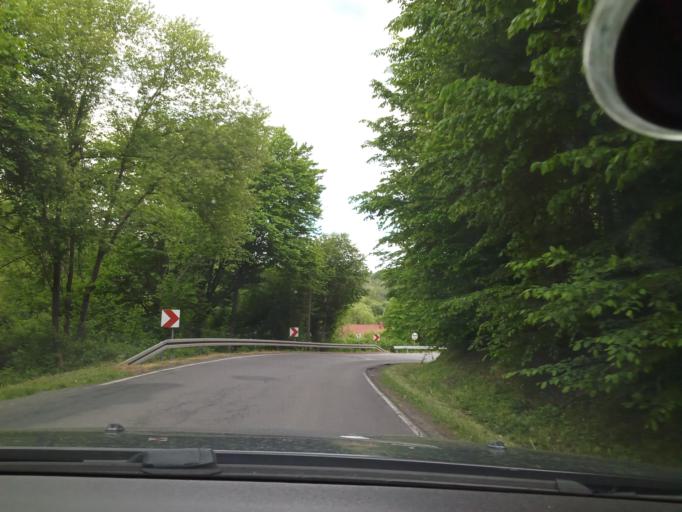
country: PL
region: Lesser Poland Voivodeship
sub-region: Powiat limanowski
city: Tymbark
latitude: 49.7513
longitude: 20.3509
